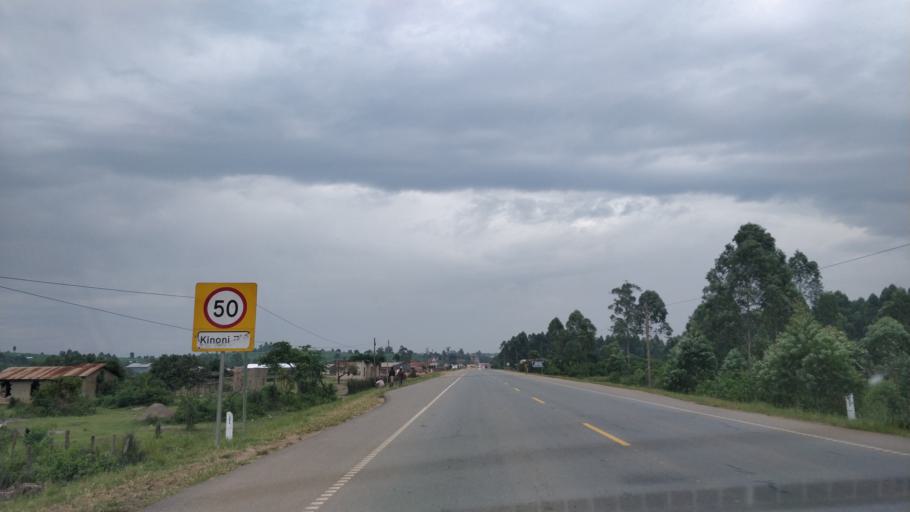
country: UG
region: Western Region
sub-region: Sheema District
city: Kibingo
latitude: -0.6645
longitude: 30.4497
